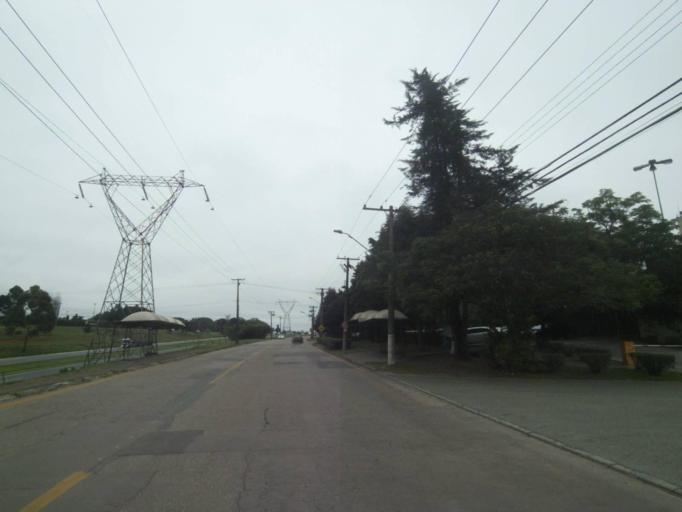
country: BR
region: Parana
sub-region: Araucaria
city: Araucaria
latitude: -25.5455
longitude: -49.3175
